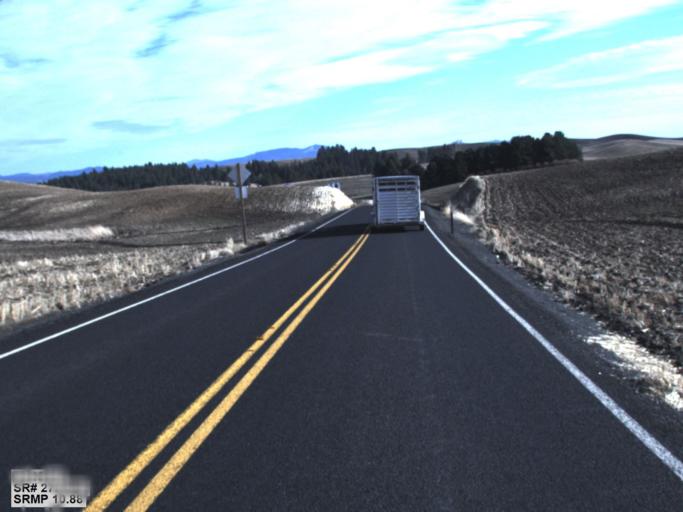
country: US
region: Washington
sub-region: Whitman County
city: Colfax
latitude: 46.9394
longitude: -117.1690
